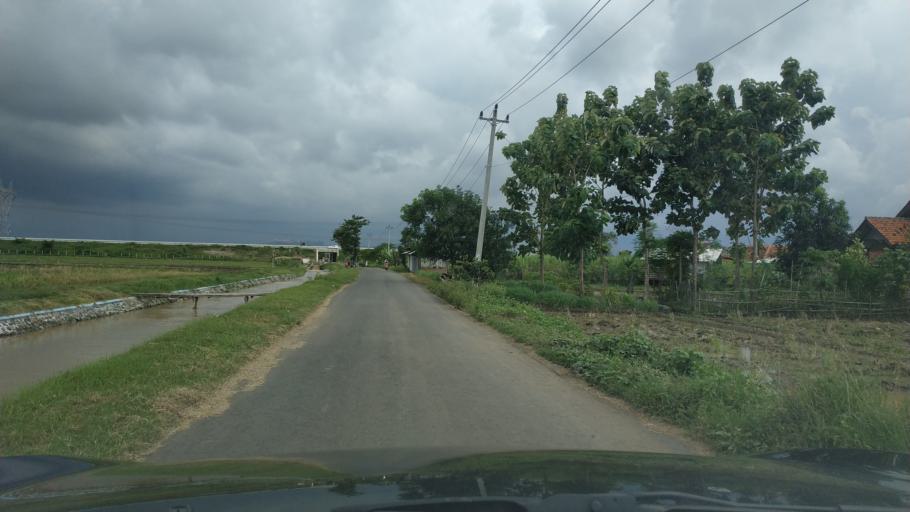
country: ID
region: Central Java
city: Pemalang
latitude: -6.9340
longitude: 109.3368
